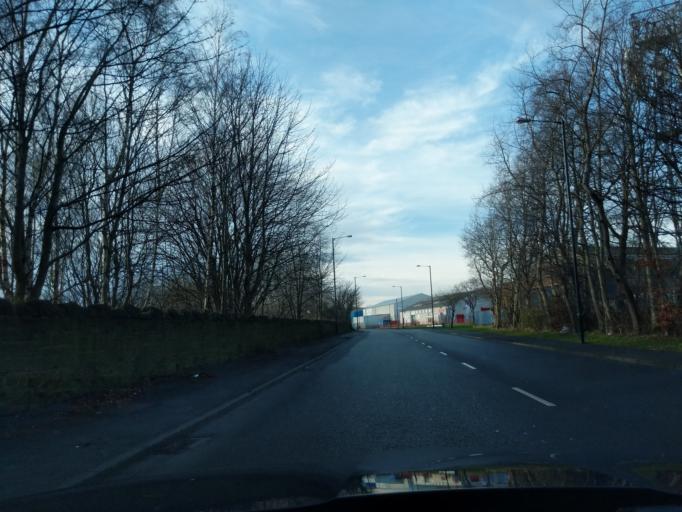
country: GB
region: England
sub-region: Borough of North Tyneside
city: Wallsend
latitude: 54.9903
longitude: -1.5228
